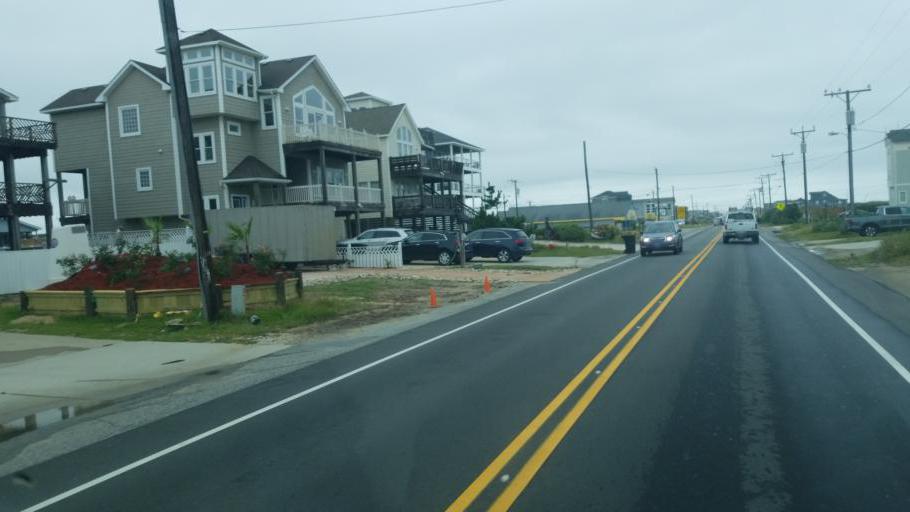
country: US
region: North Carolina
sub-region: Dare County
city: Kill Devil Hills
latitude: 36.0423
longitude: -75.6742
